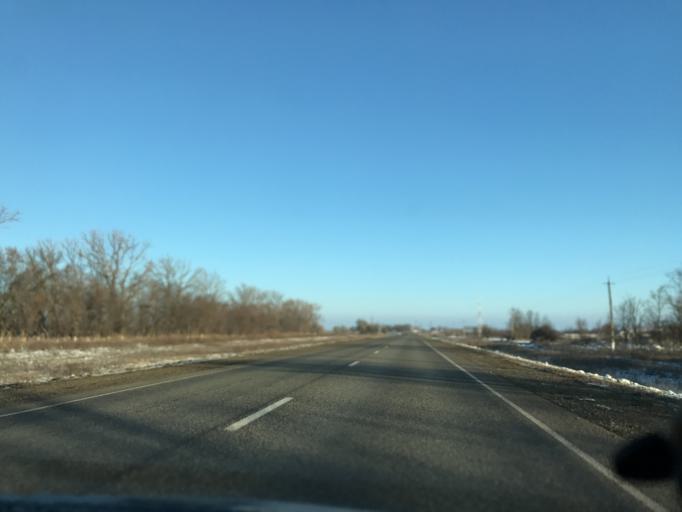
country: RU
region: Stavropol'skiy
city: Bezopasnoye
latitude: 45.6081
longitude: 41.9417
